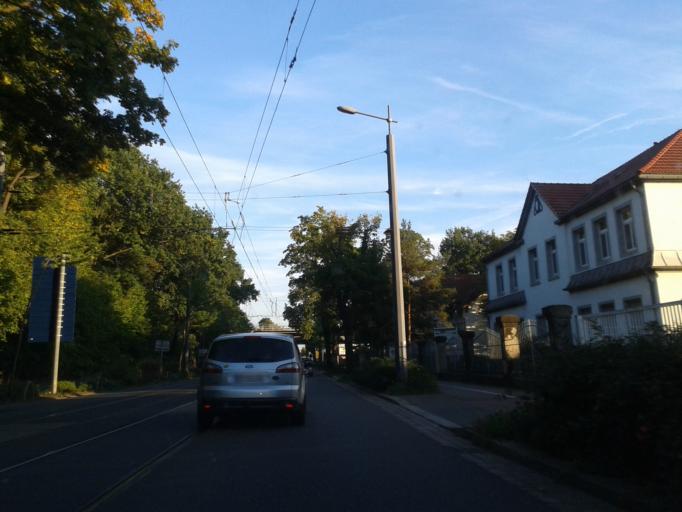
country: DE
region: Saxony
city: Radebeul
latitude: 51.0956
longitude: 13.6952
